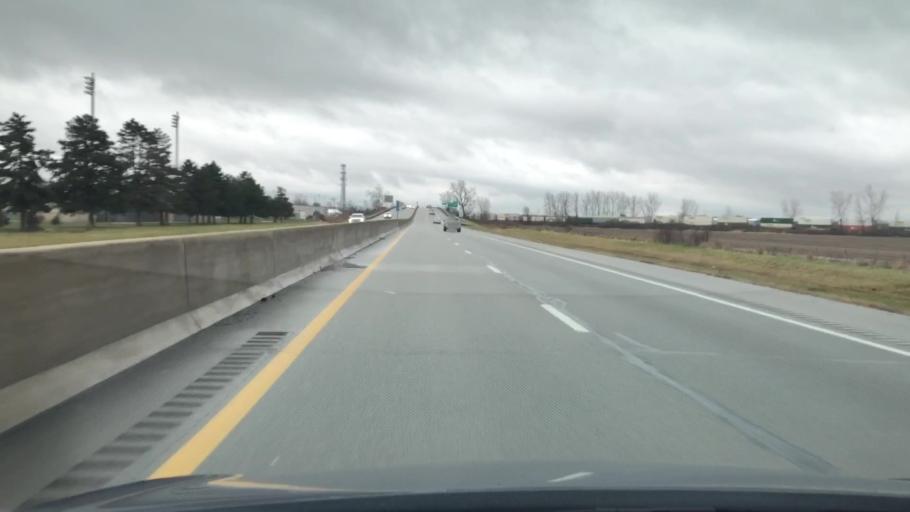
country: US
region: Ohio
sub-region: Wood County
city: Northwood
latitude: 41.6042
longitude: -83.4770
